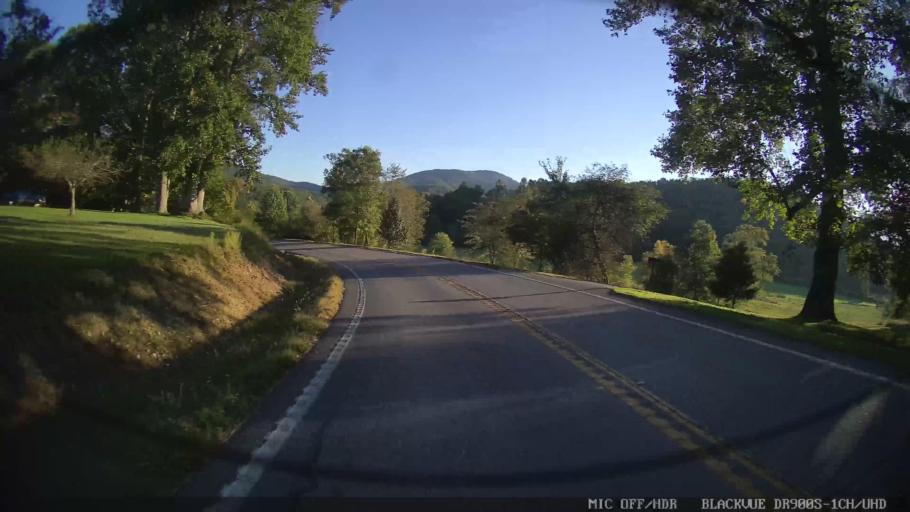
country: US
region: Georgia
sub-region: Fannin County
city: Blue Ridge
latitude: 34.8414
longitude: -84.1926
